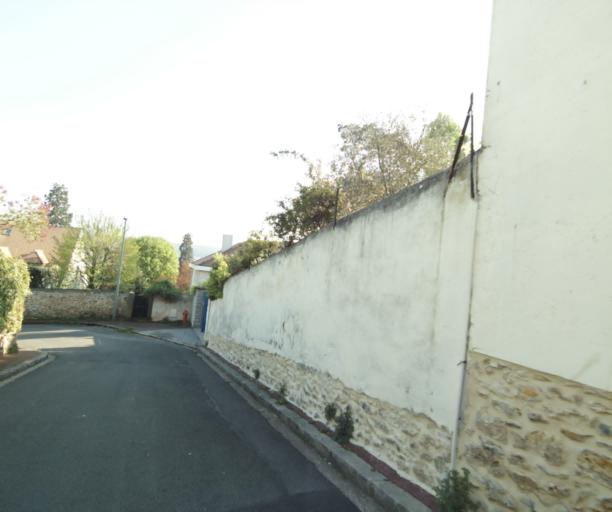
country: FR
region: Ile-de-France
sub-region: Departement des Hauts-de-Seine
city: Ville-d'Avray
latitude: 48.8290
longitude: 2.2044
